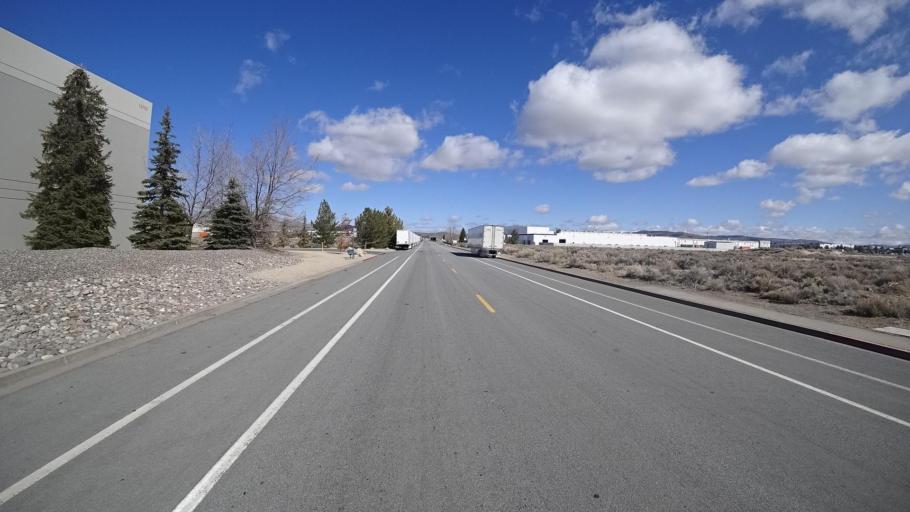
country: US
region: Nevada
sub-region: Washoe County
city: Lemmon Valley
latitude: 39.6511
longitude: -119.8970
